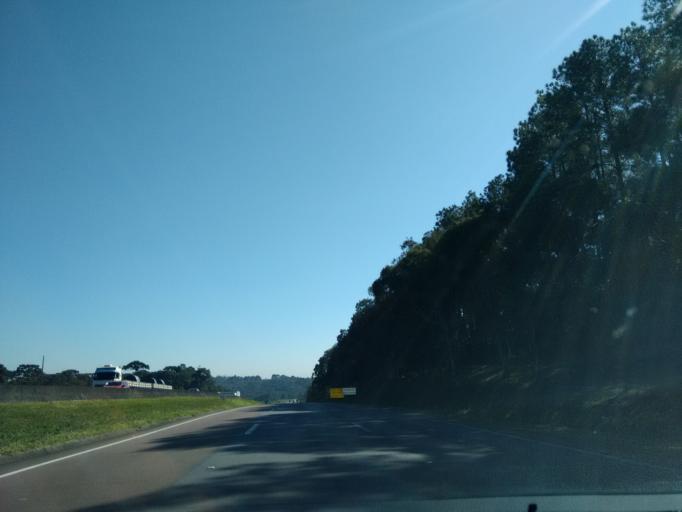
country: BR
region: Parana
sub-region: Sao Jose Dos Pinhais
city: Sao Jose dos Pinhais
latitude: -25.8144
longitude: -49.1313
